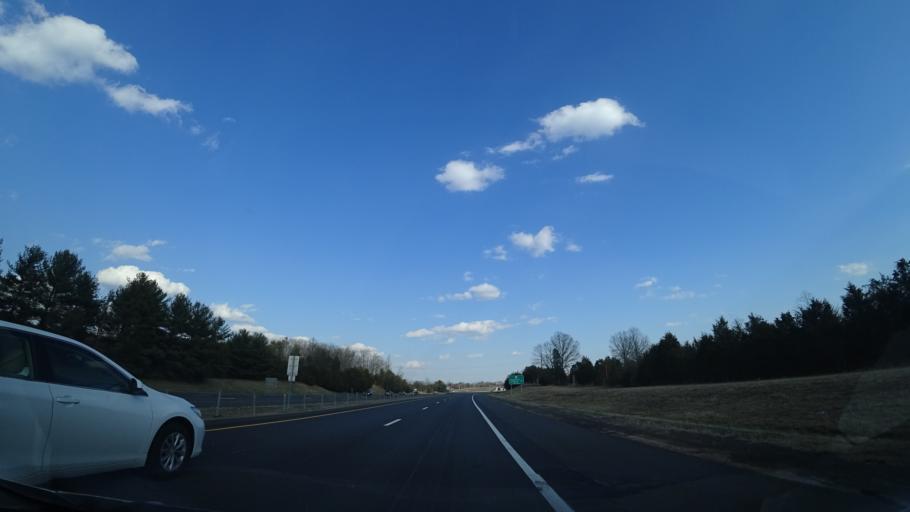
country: US
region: Virginia
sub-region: Prince William County
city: Haymarket
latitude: 38.8206
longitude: -77.6484
